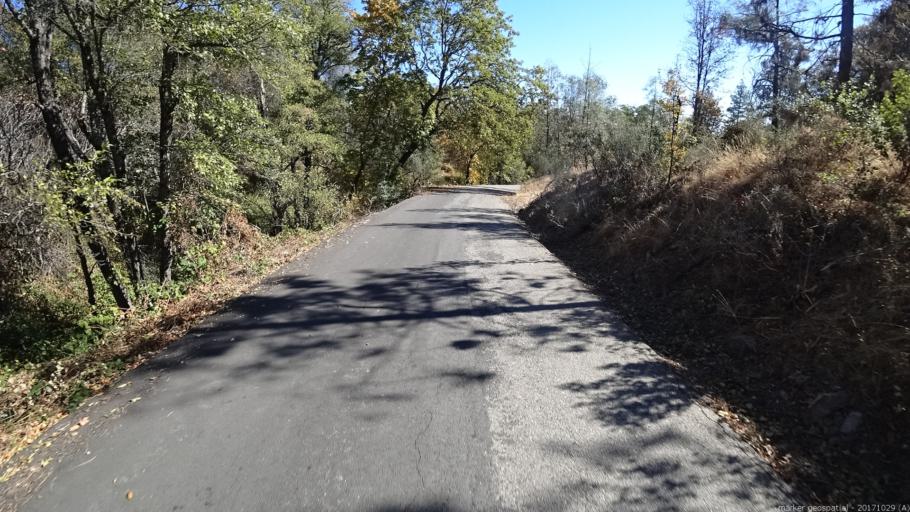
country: US
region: California
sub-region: Shasta County
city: Shasta
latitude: 40.4907
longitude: -122.6854
